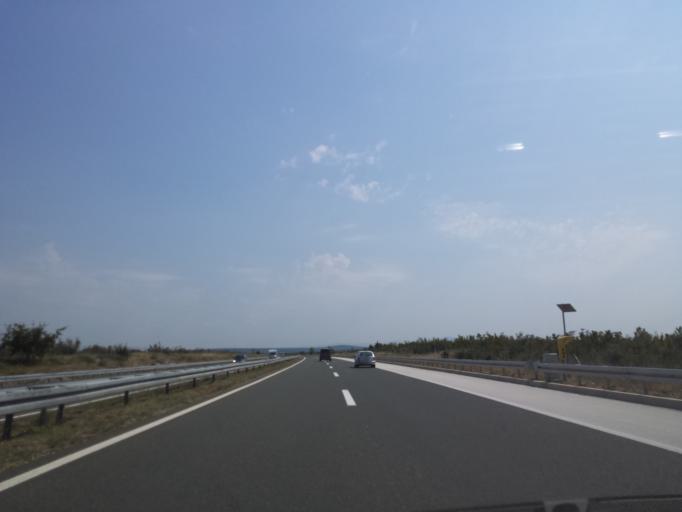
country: HR
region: Sibensko-Kniniska
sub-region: Grad Sibenik
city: Pirovac
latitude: 43.9069
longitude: 15.7594
